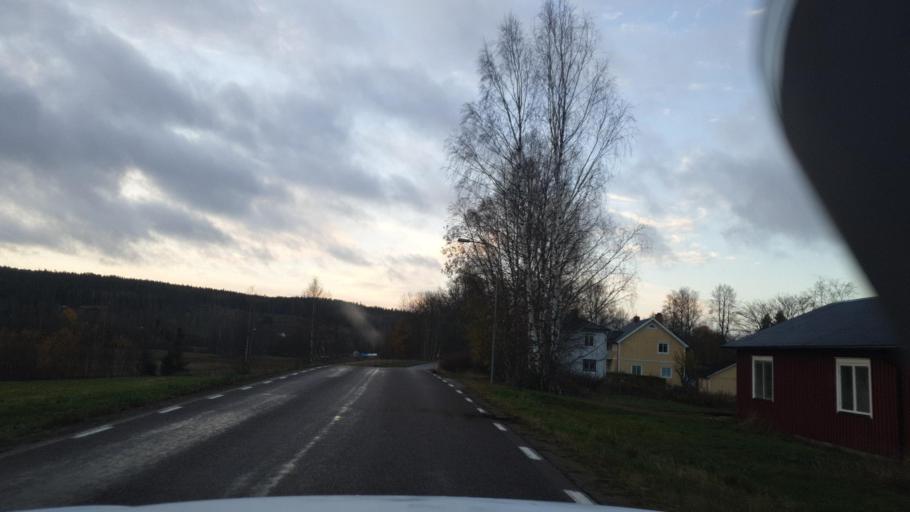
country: SE
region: Vaermland
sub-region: Arvika Kommun
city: Arvika
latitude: 59.6026
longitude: 12.7595
